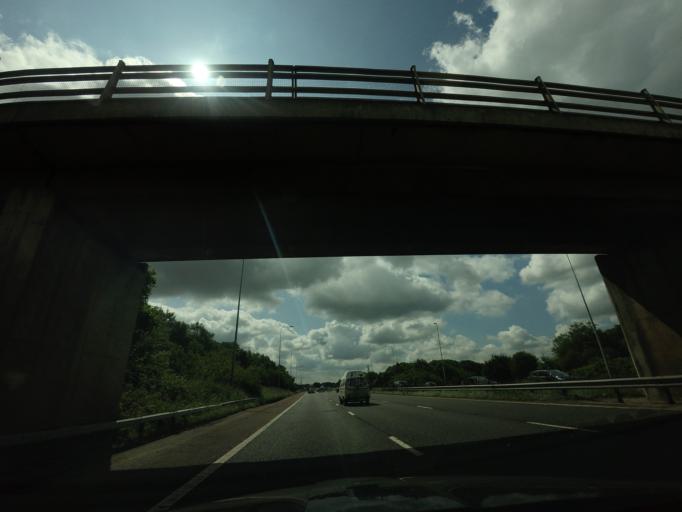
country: GB
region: England
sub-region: Lancashire
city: Coppull
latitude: 53.6077
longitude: -2.6884
